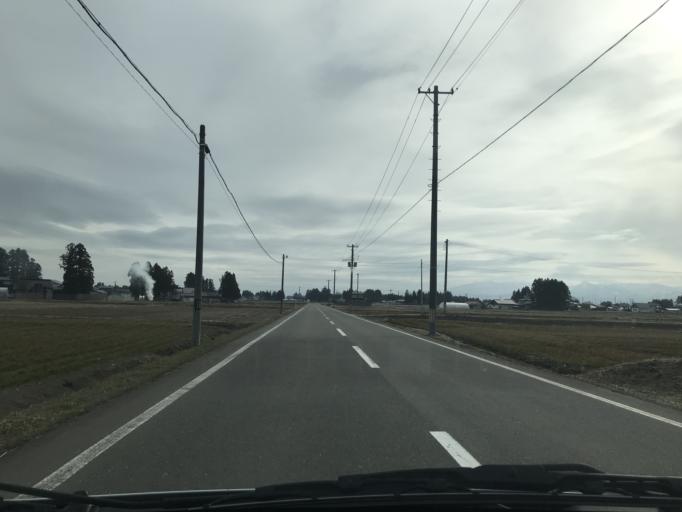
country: JP
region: Iwate
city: Hanamaki
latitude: 39.3639
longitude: 141.0677
